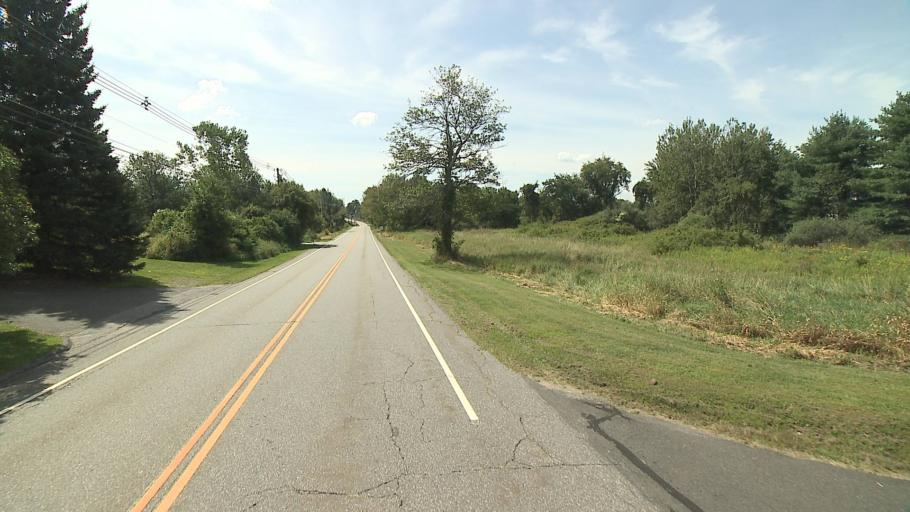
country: US
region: Connecticut
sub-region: Litchfield County
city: Bethlehem Village
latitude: 41.6736
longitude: -73.1972
